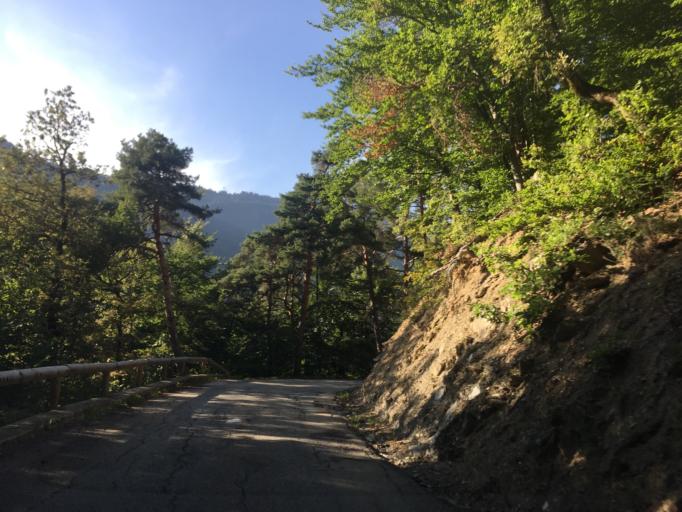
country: FR
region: Rhone-Alpes
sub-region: Departement de la Savoie
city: Moutiers
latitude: 45.5080
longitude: 6.5732
